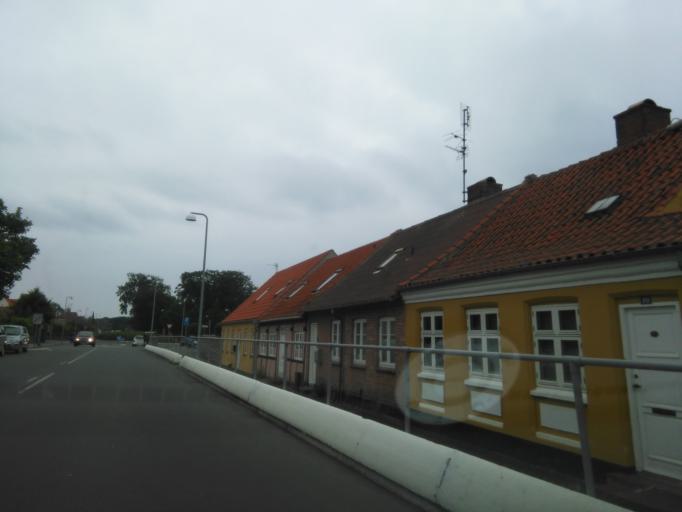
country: DK
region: Capital Region
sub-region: Bornholm Kommune
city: Ronne
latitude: 55.0956
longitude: 14.7027
